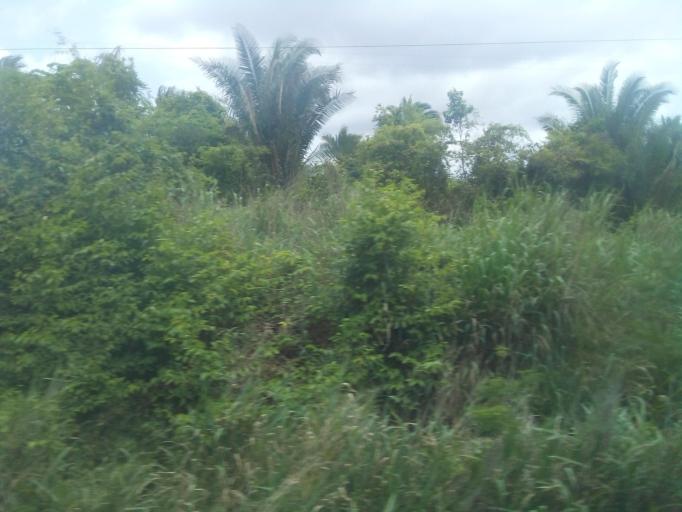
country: BR
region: Maranhao
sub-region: Santa Ines
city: Santa Ines
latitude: -3.6466
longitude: -45.7244
